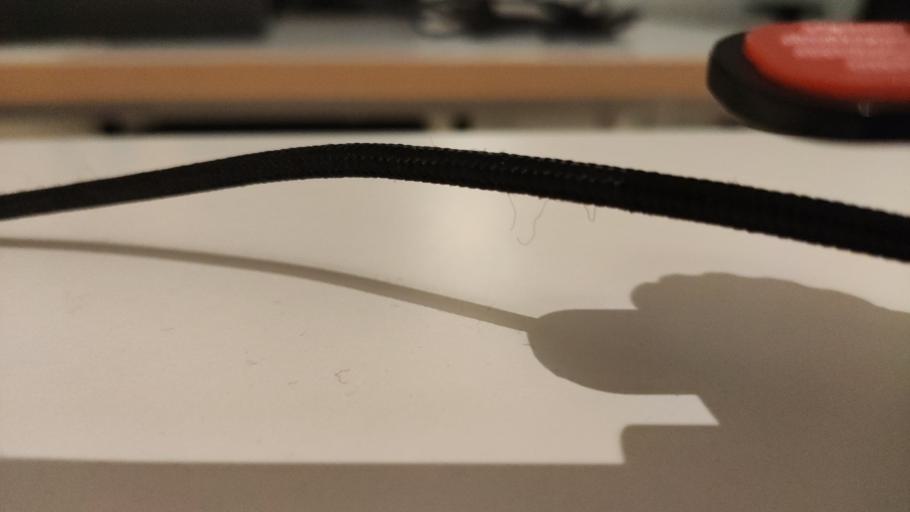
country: RU
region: Moskovskaya
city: Kurovskoye
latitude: 55.5429
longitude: 38.8731
